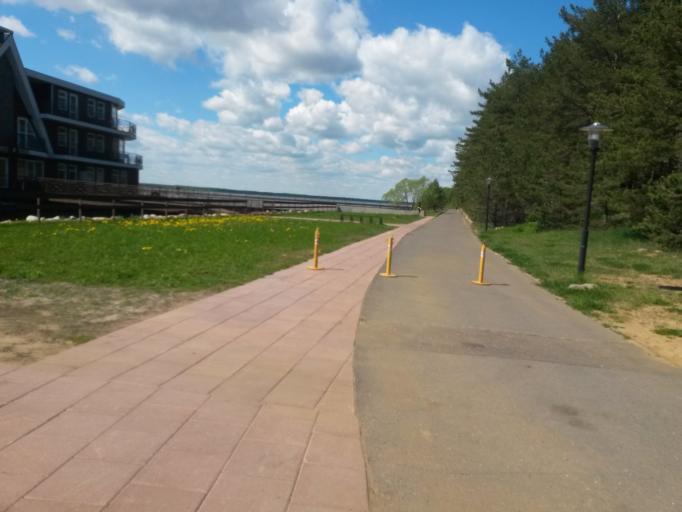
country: RU
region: Jaroslavl
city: Borok
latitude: 58.0611
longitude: 38.3510
